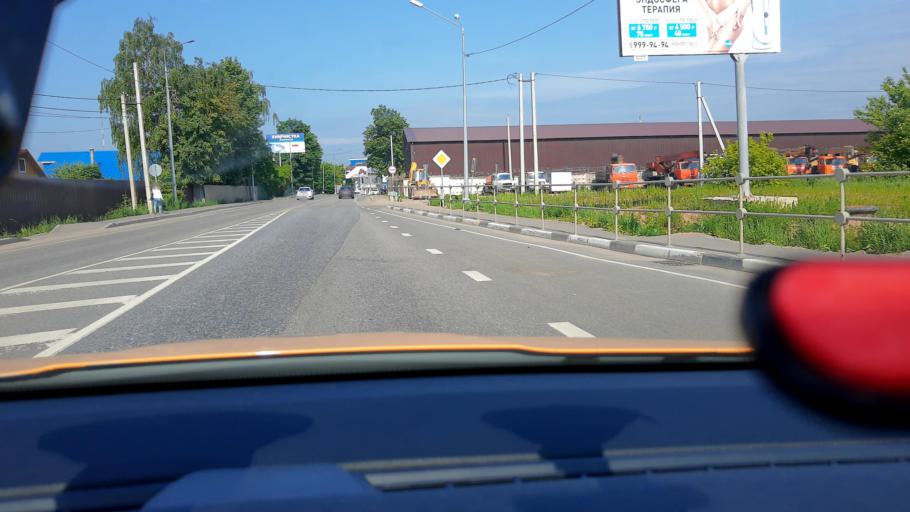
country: RU
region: Moskovskaya
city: Rozhdestveno
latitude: 55.8092
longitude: 37.0176
